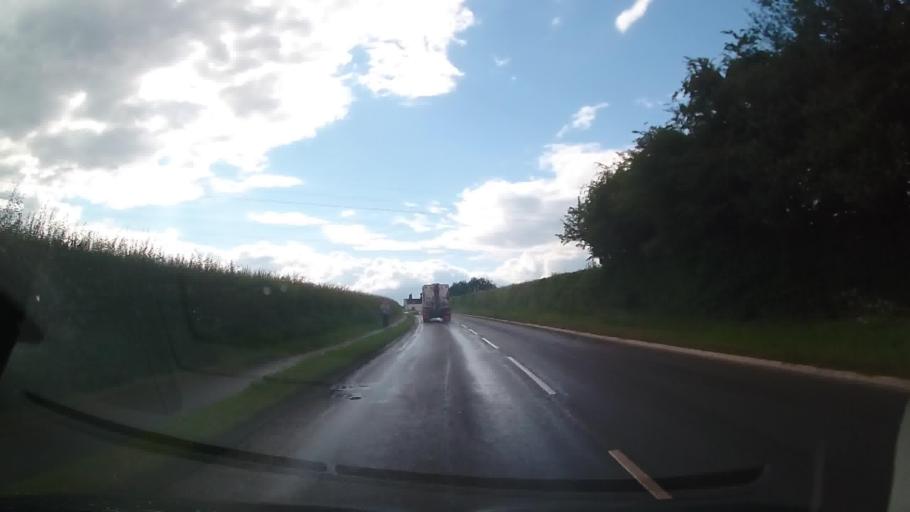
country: GB
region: England
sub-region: Telford and Wrekin
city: Ironbridge
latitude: 52.6612
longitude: -2.4928
